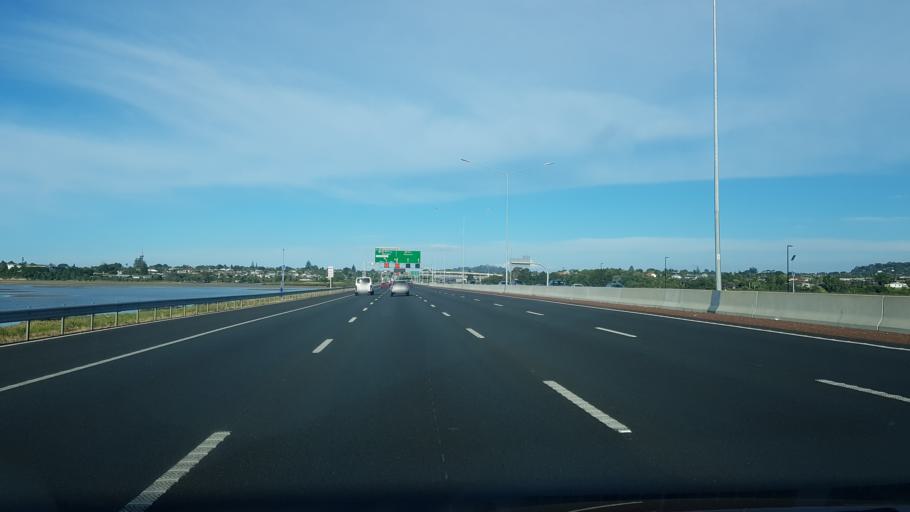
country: NZ
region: Auckland
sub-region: Auckland
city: Rosebank
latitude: -36.8718
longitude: 174.6860
